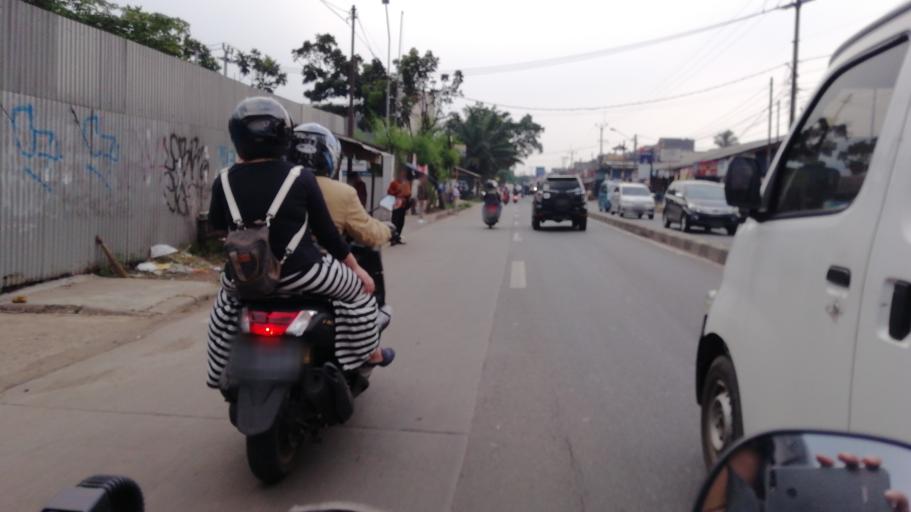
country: ID
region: West Java
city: Ciampea
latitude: -6.5136
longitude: 106.7573
